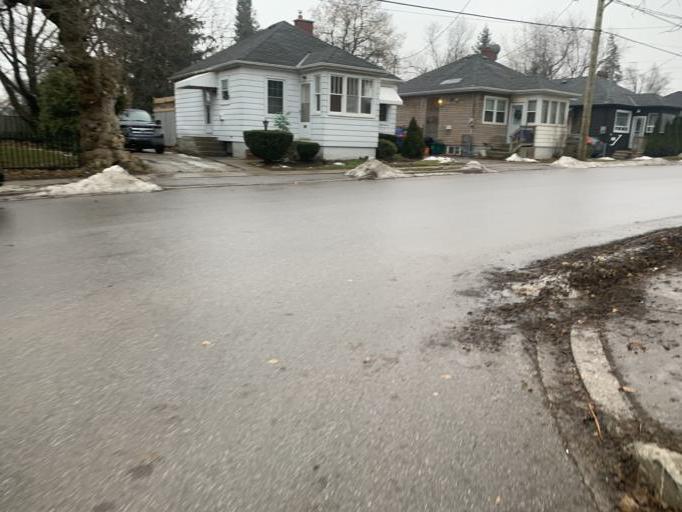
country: CA
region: Ontario
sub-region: Halton
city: Milton
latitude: 43.6546
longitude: -79.9312
